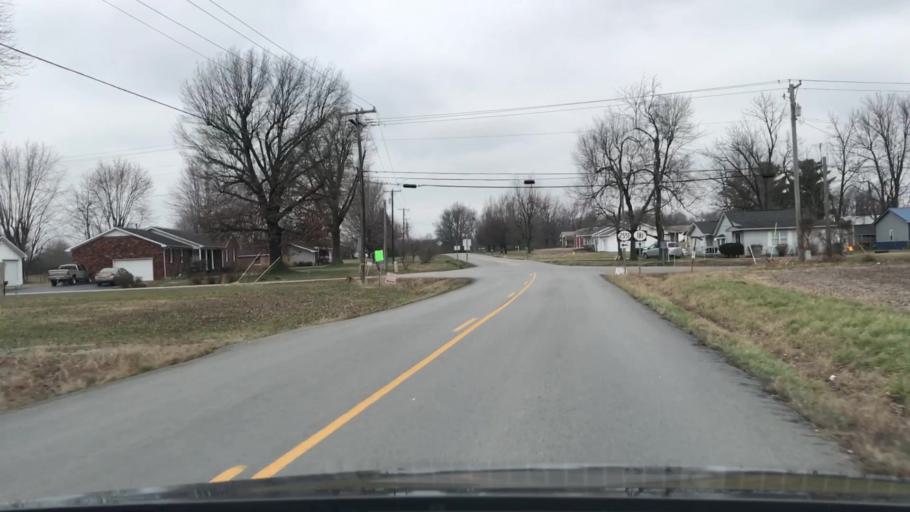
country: US
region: Kentucky
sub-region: Muhlenberg County
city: Morehead
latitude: 37.3562
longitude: -87.2294
